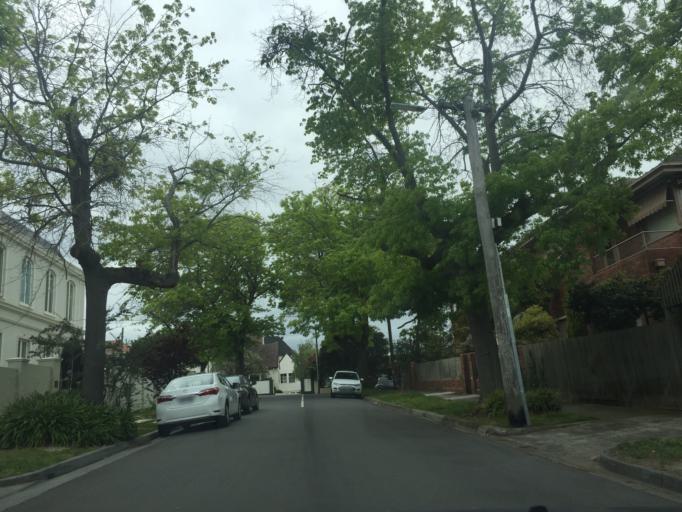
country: AU
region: Victoria
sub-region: Boroondara
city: Hawthorn East
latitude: -37.8174
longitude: 145.0547
